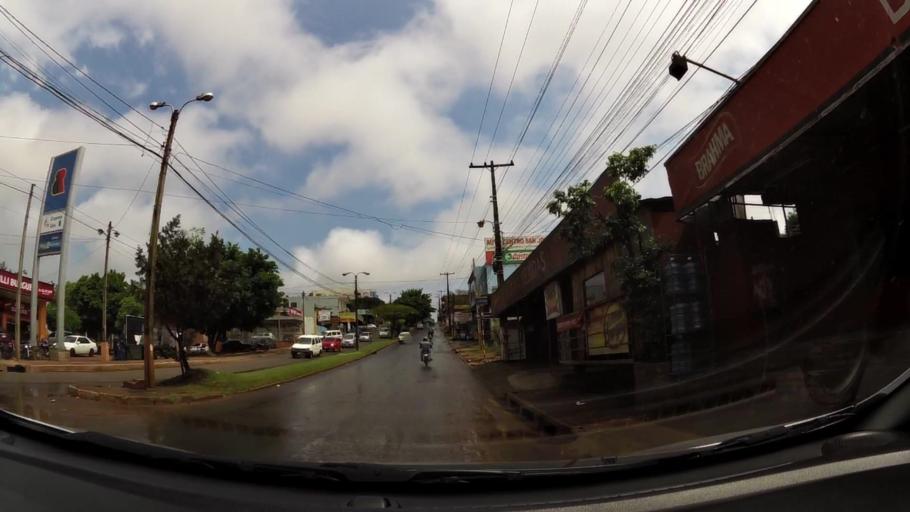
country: PY
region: Alto Parana
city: Ciudad del Este
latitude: -25.5104
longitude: -54.6594
